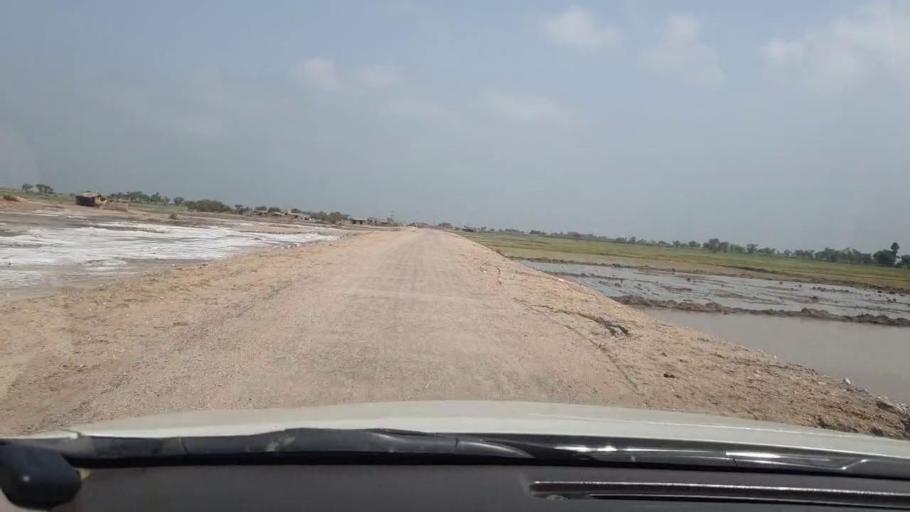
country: PK
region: Sindh
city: Shikarpur
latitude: 28.0039
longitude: 68.5576
